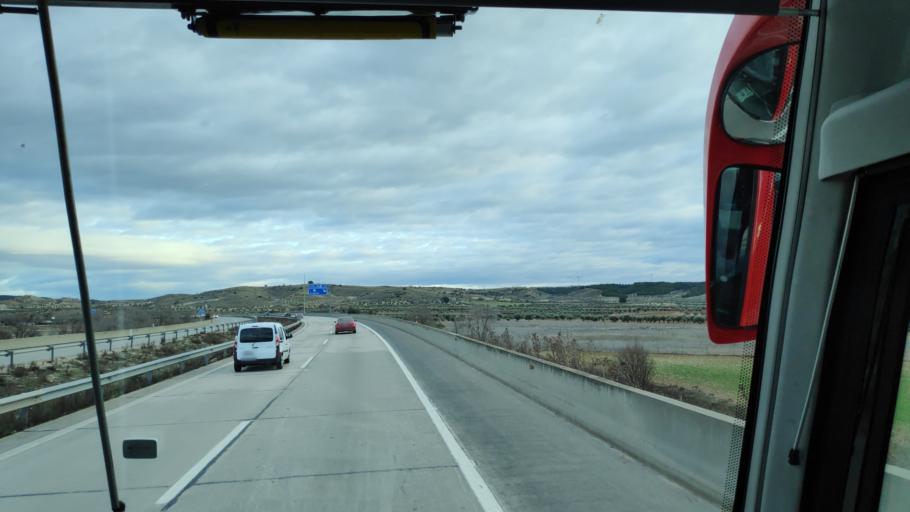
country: ES
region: Madrid
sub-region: Provincia de Madrid
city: Vaciamadrid
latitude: 40.3012
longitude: -3.4846
